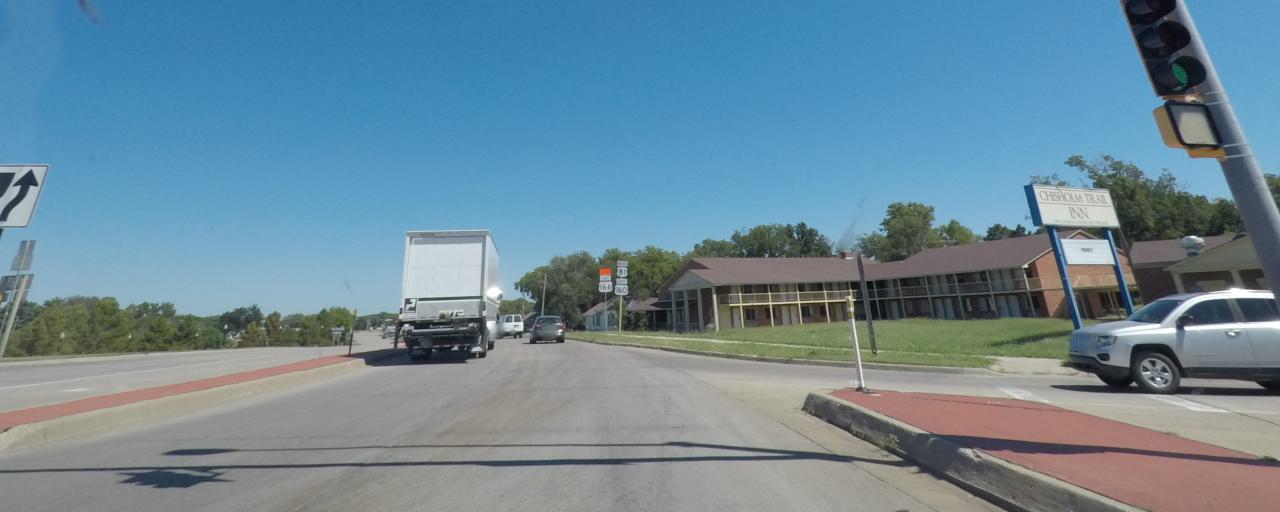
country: US
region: Kansas
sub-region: Sumner County
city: Wellington
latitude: 37.2677
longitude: -97.4023
